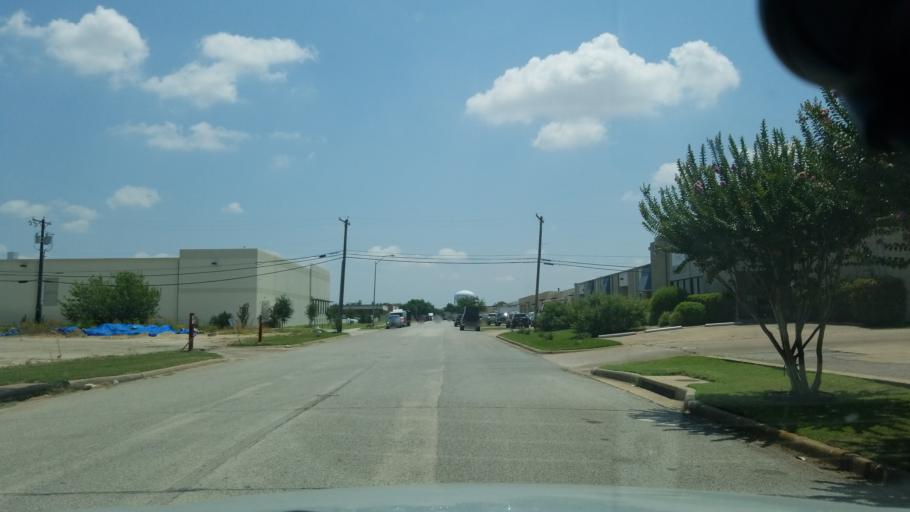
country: US
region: Texas
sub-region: Dallas County
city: Carrollton
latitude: 32.9515
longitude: -96.8677
